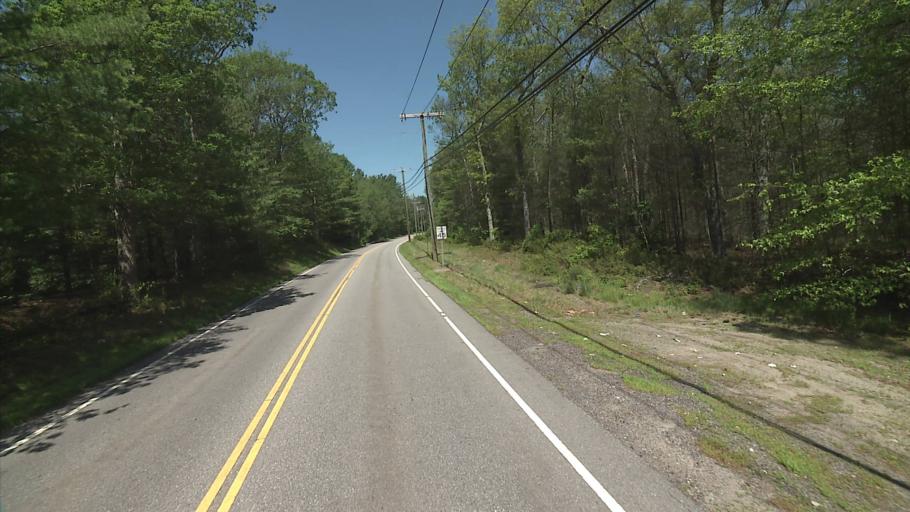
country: US
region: Connecticut
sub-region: Windham County
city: Moosup
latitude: 41.7087
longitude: -71.8404
